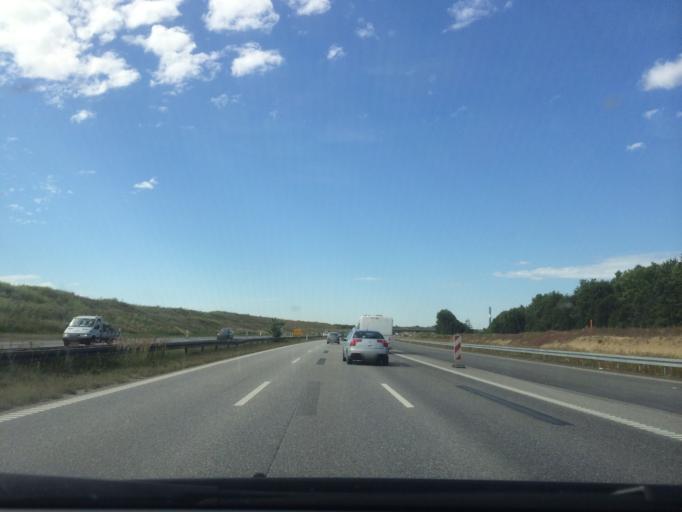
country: DK
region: Zealand
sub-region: Solrod Kommune
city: Solrod Strand
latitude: 55.5506
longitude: 12.2236
